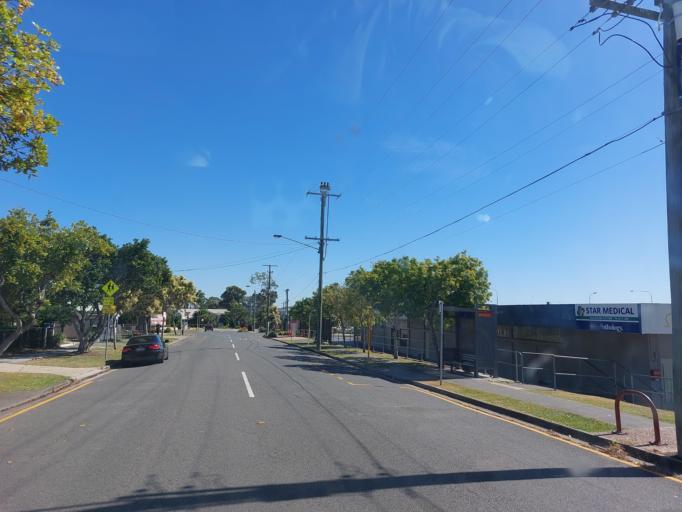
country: AU
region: Queensland
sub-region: Brisbane
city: Sunnybank
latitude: -27.5903
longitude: 153.0265
